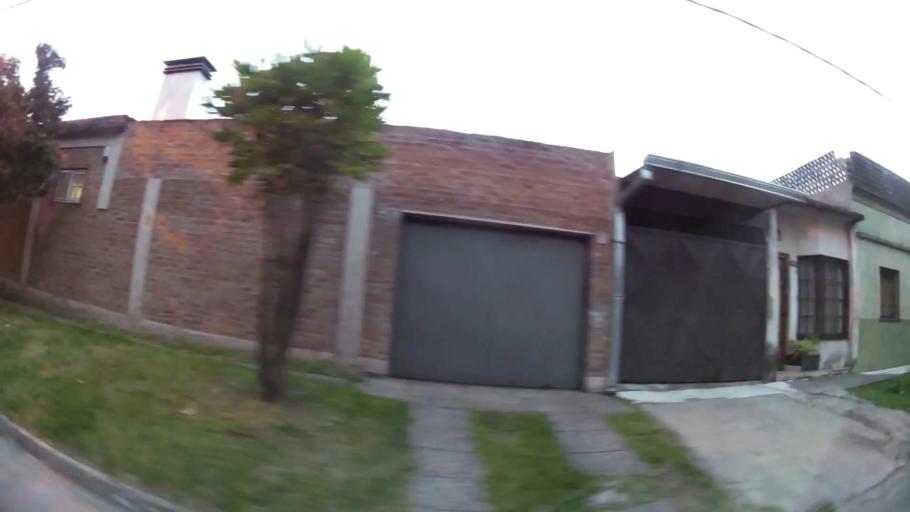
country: AR
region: Buenos Aires
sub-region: Partido de Quilmes
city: Quilmes
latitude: -34.7447
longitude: -58.2310
